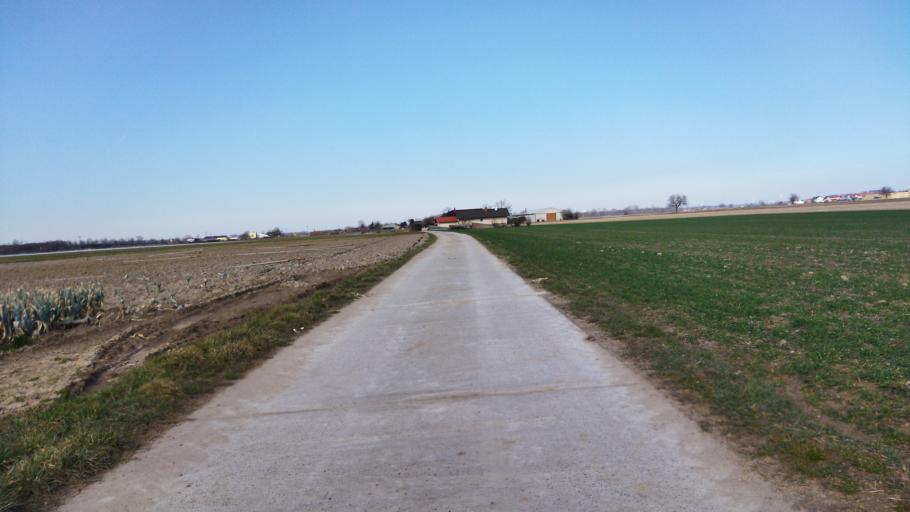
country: DE
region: Rheinland-Pfalz
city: Waldsee
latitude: 49.3822
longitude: 8.4281
